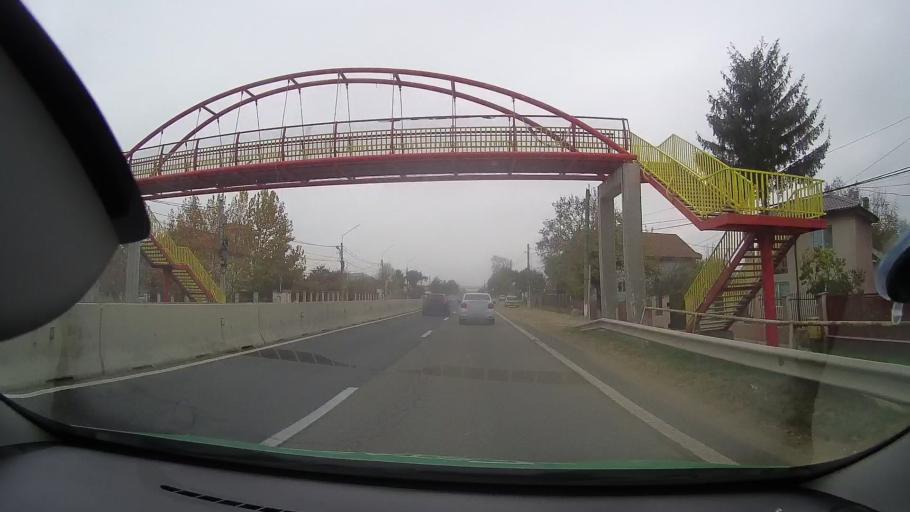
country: RO
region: Ilfov
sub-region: Comuna Corbeanca
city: Corbeanca
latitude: 44.6267
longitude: 26.0692
